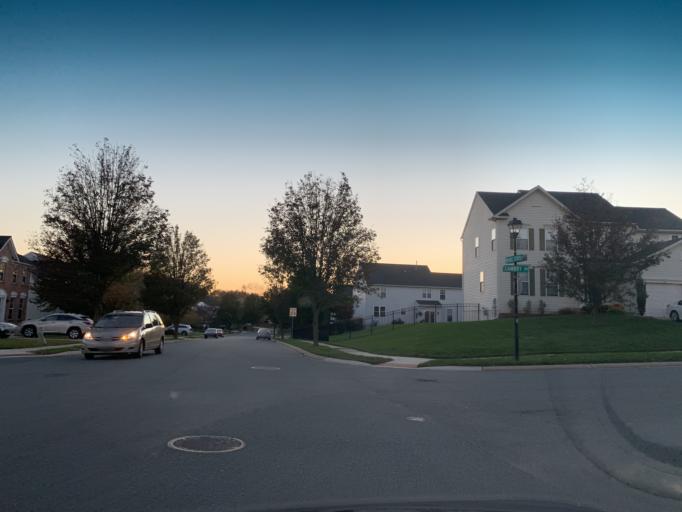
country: US
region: Maryland
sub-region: Harford County
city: Bel Air South
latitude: 39.5319
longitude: -76.3043
